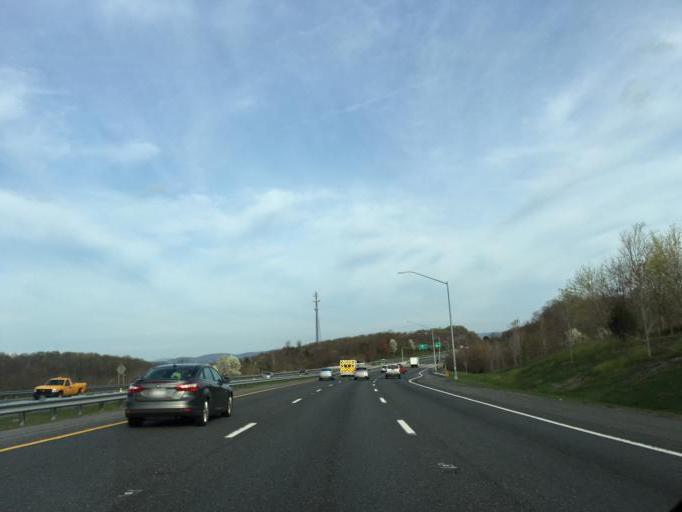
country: US
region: Maryland
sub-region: Frederick County
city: Spring Ridge
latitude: 39.3920
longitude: -77.3235
